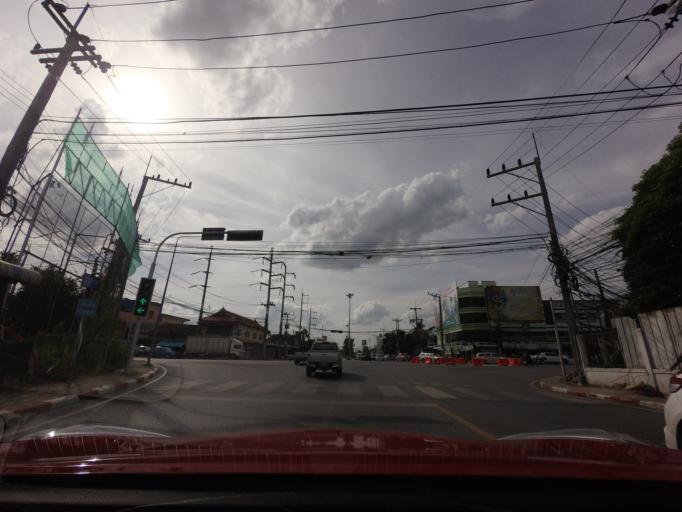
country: TH
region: Yala
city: Yala
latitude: 6.5475
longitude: 101.2757
